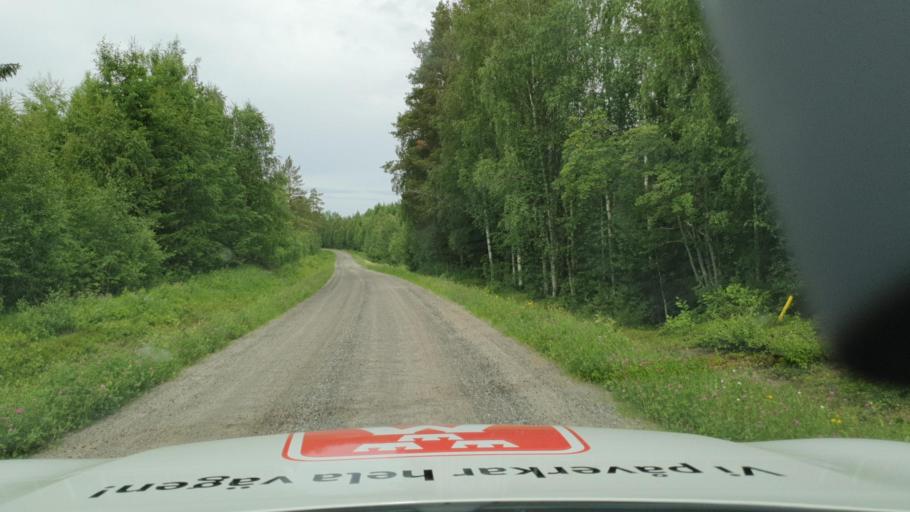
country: SE
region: Vaesterbotten
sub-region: Robertsfors Kommun
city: Robertsfors
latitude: 64.1969
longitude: 20.7098
